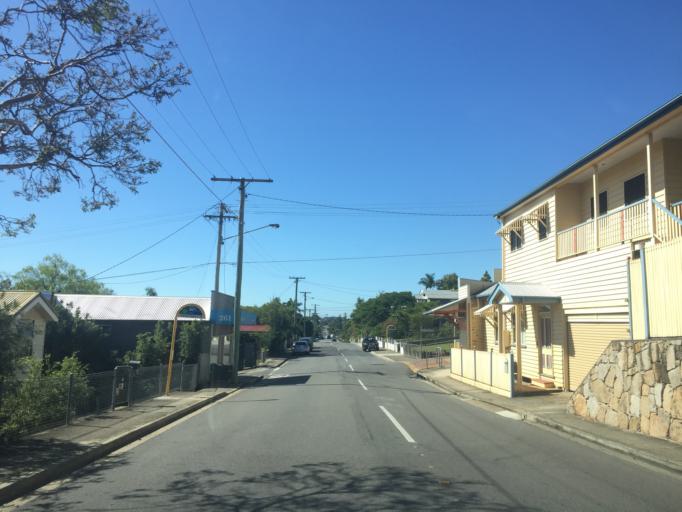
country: AU
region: Queensland
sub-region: Brisbane
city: Grange
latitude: -27.4254
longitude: 153.0111
